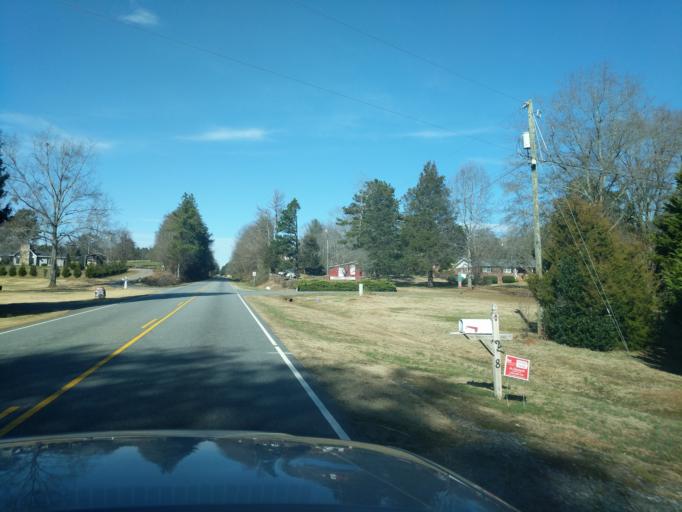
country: US
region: North Carolina
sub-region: Rutherford County
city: Rutherfordton
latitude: 35.3906
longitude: -81.9602
